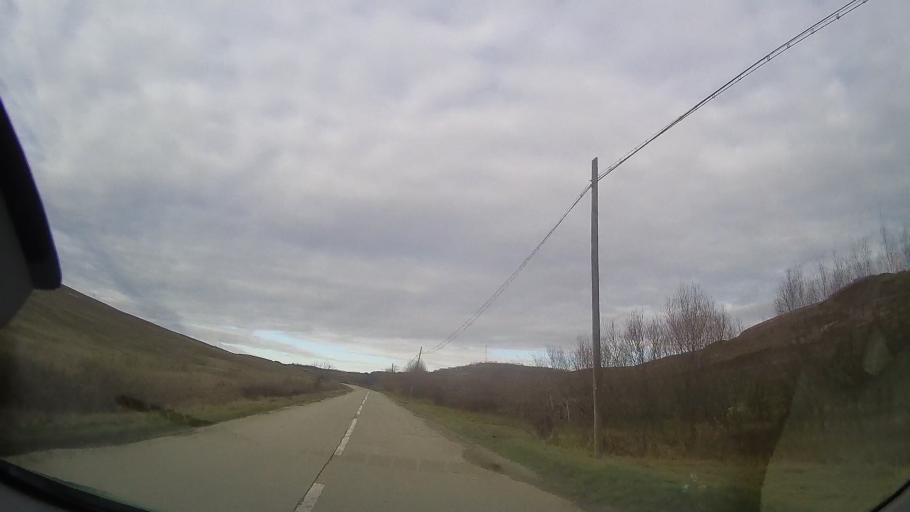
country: RO
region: Bistrita-Nasaud
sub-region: Comuna Micestii de Campie
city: Micestii de Campie
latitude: 46.8398
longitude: 24.3038
